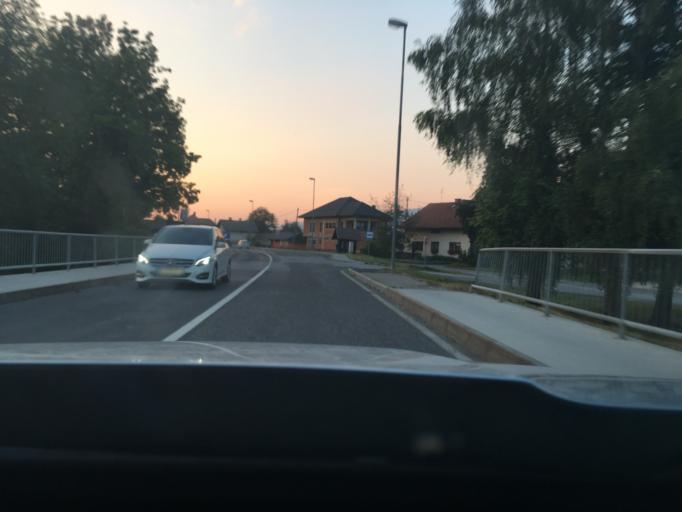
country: SI
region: Ribnica
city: Ribnica
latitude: 45.7309
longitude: 14.7366
